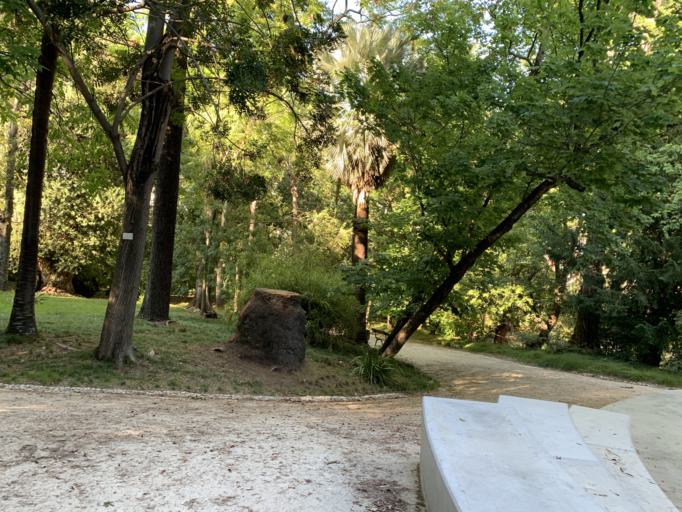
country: PT
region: Lisbon
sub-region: Lisbon
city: Lisbon
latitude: 38.7186
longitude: -9.1486
